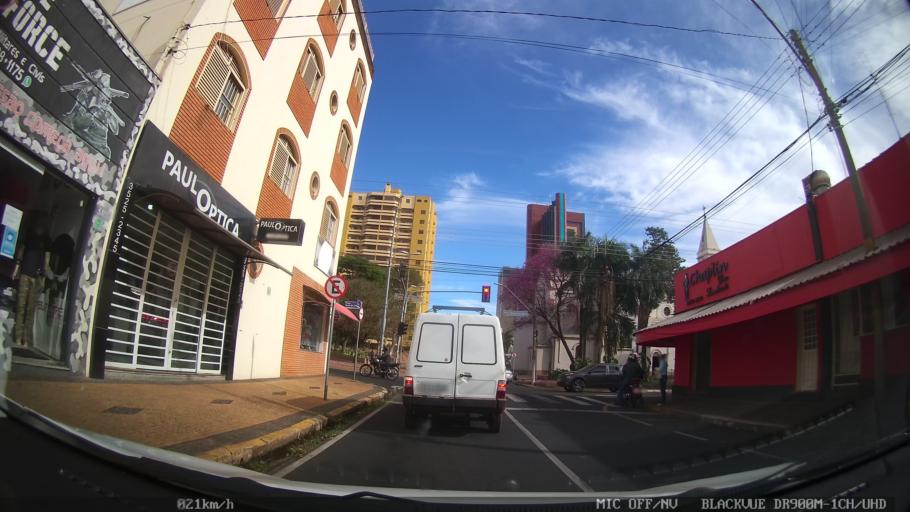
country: BR
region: Sao Paulo
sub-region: Catanduva
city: Catanduva
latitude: -21.1389
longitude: -48.9725
